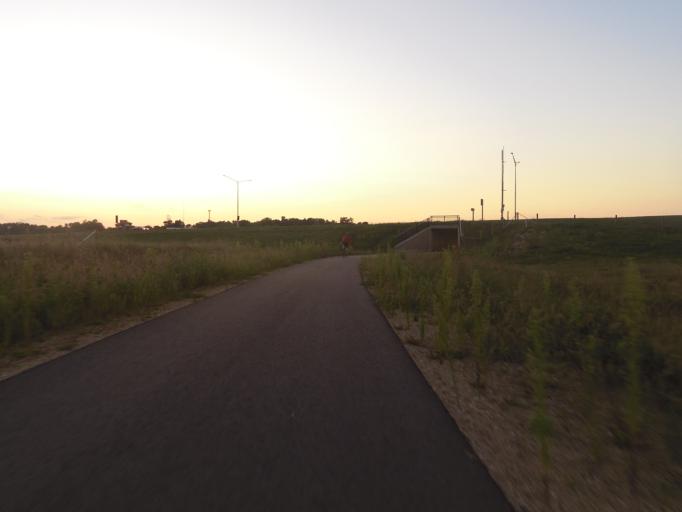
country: US
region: Minnesota
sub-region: Washington County
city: Stillwater
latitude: 45.0586
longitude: -92.7827
